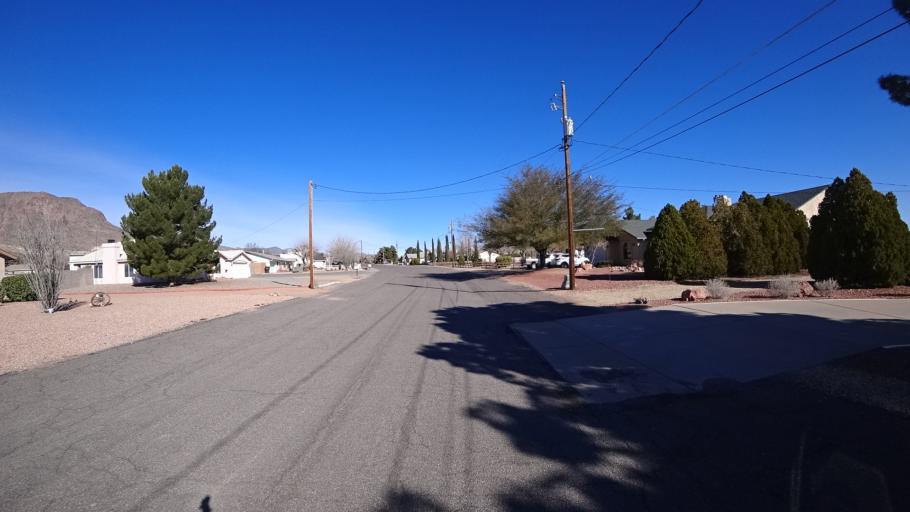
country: US
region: Arizona
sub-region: Mohave County
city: New Kingman-Butler
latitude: 35.2610
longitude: -114.0411
